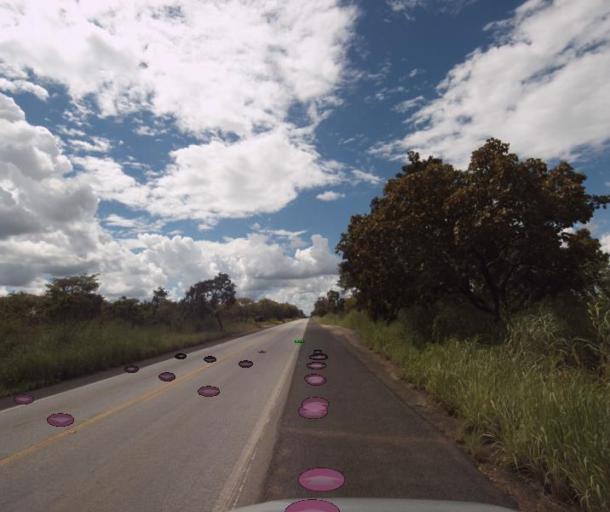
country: BR
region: Goias
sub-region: Porangatu
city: Porangatu
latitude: -13.8625
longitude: -49.0506
